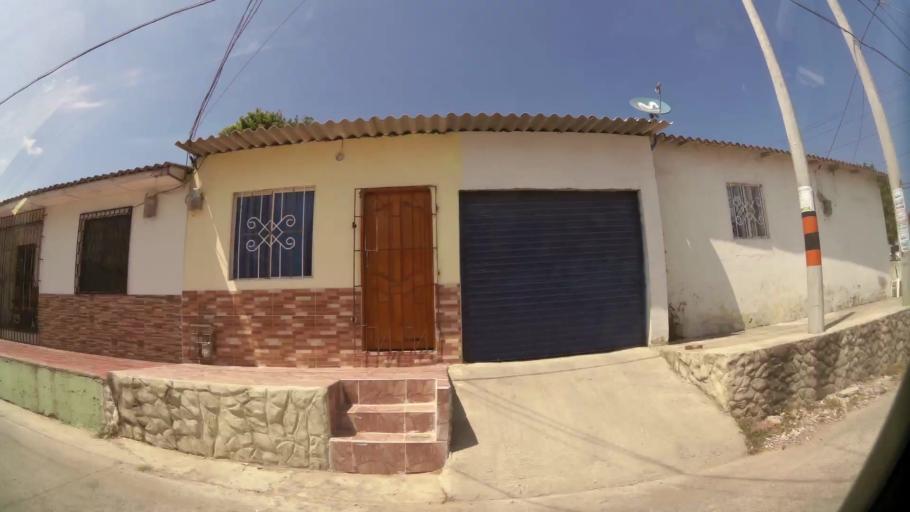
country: CO
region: Atlantico
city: Barranquilla
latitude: 10.9613
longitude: -74.8086
